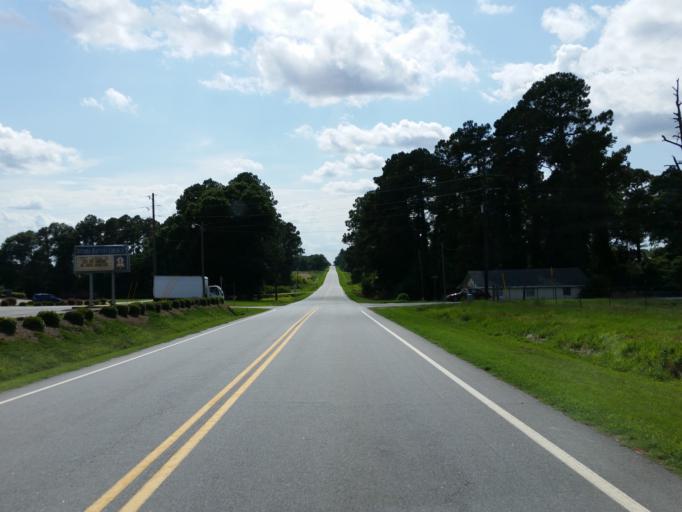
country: US
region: Georgia
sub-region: Turner County
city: Ashburn
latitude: 31.6587
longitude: -83.5654
